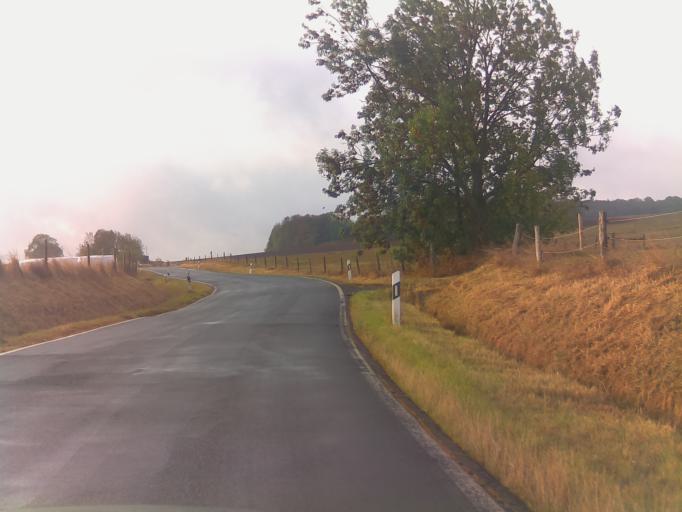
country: DE
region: Hesse
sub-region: Regierungsbezirk Giessen
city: Freiensteinau
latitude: 50.4811
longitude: 9.4020
